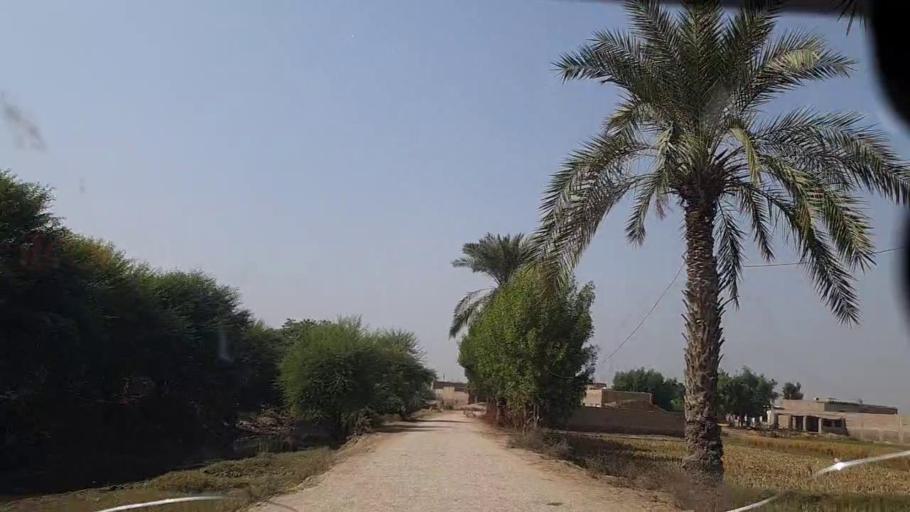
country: PK
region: Sindh
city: Shikarpur
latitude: 27.9868
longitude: 68.6332
